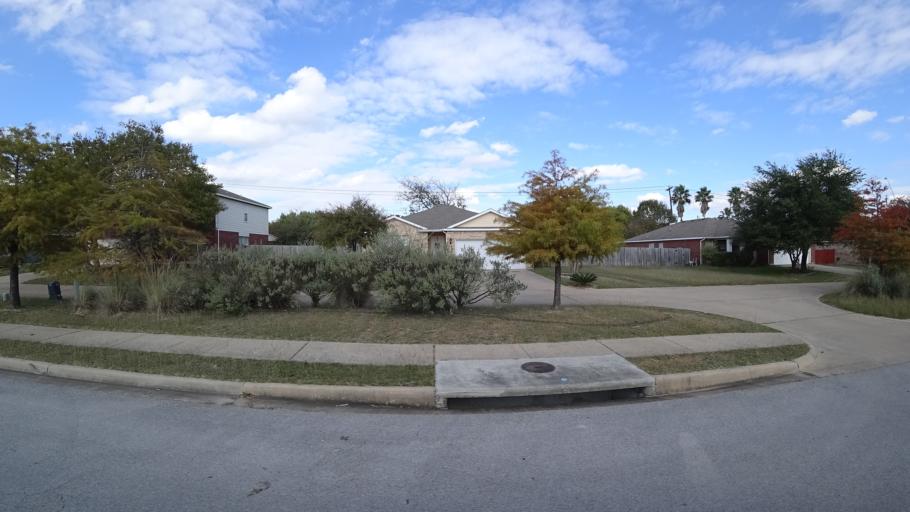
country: US
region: Texas
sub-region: Travis County
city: Pflugerville
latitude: 30.4346
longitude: -97.6357
